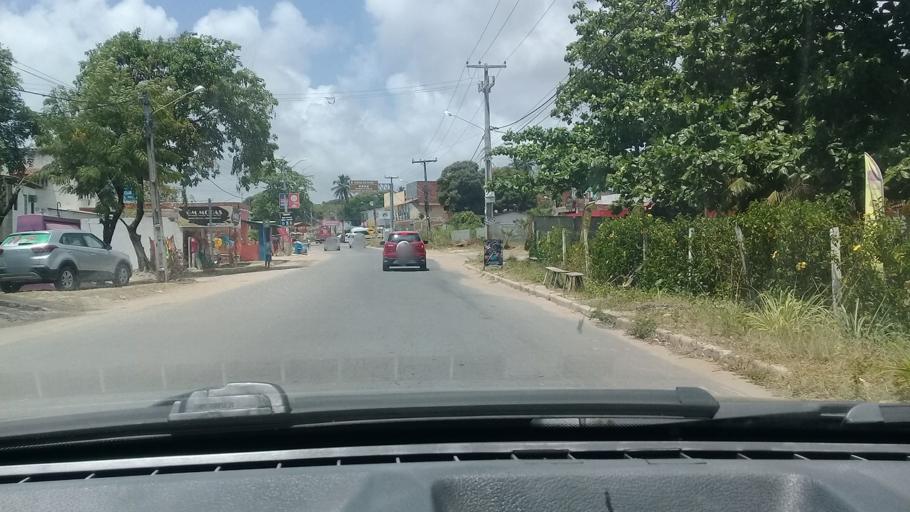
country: BR
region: Pernambuco
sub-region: Itamaraca
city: Itamaraca
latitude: -7.7853
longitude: -34.8393
